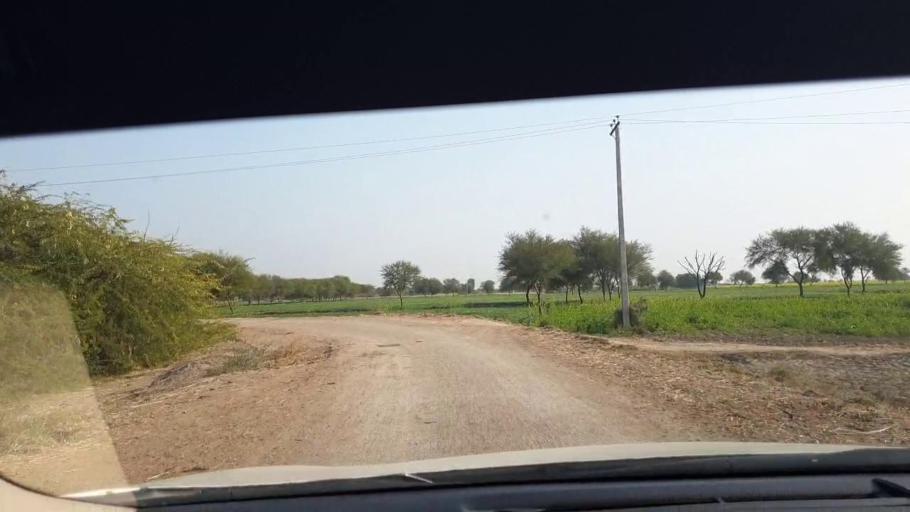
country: PK
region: Sindh
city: Berani
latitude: 25.8124
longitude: 68.7779
